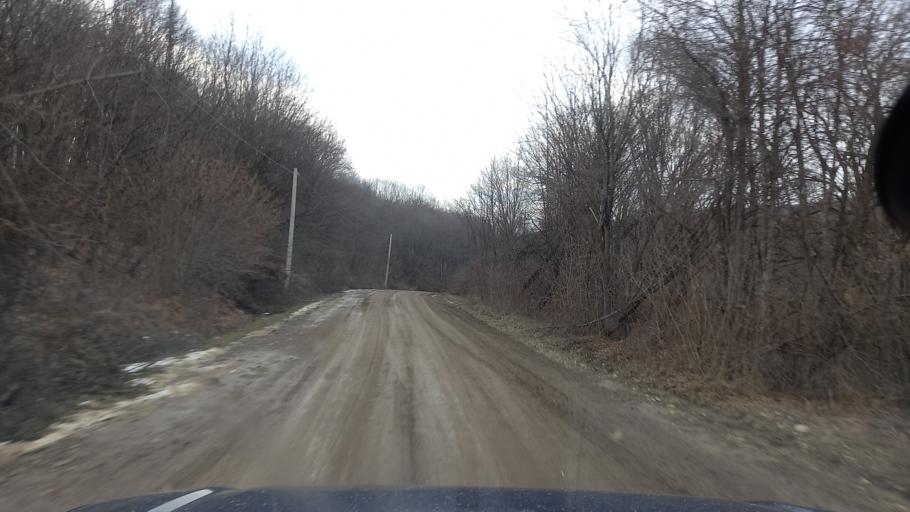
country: RU
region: Adygeya
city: Kamennomostskiy
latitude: 44.1396
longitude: 40.2849
